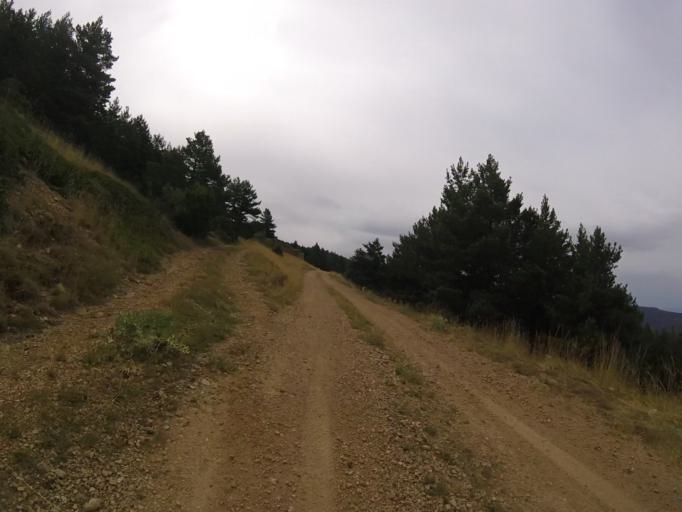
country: ES
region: Aragon
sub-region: Provincia de Teruel
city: Valdelinares
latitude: 40.3574
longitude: -0.5999
